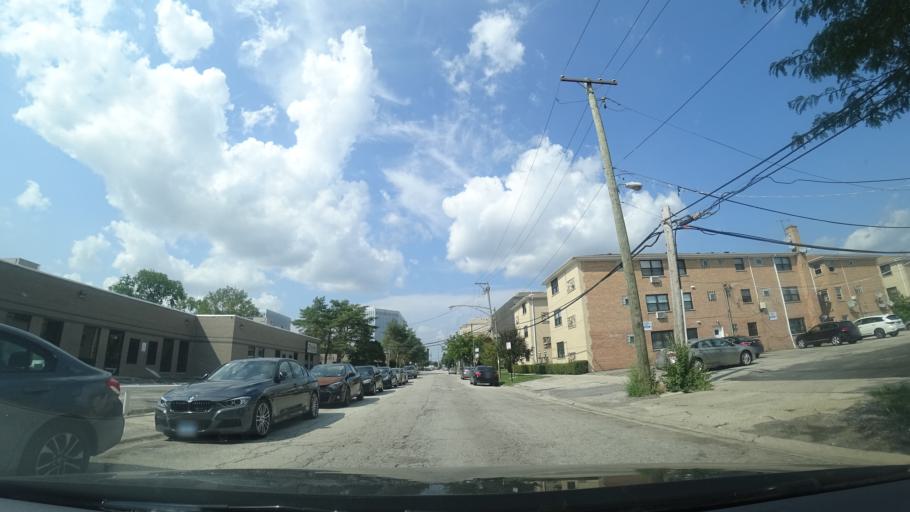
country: US
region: Illinois
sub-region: Cook County
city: Norridge
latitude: 41.9796
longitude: -87.8412
